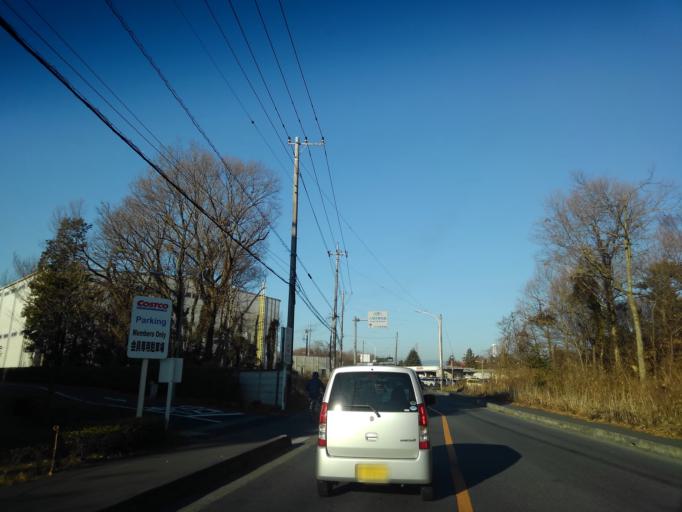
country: JP
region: Saitama
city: Sayama
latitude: 35.8123
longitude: 139.3805
